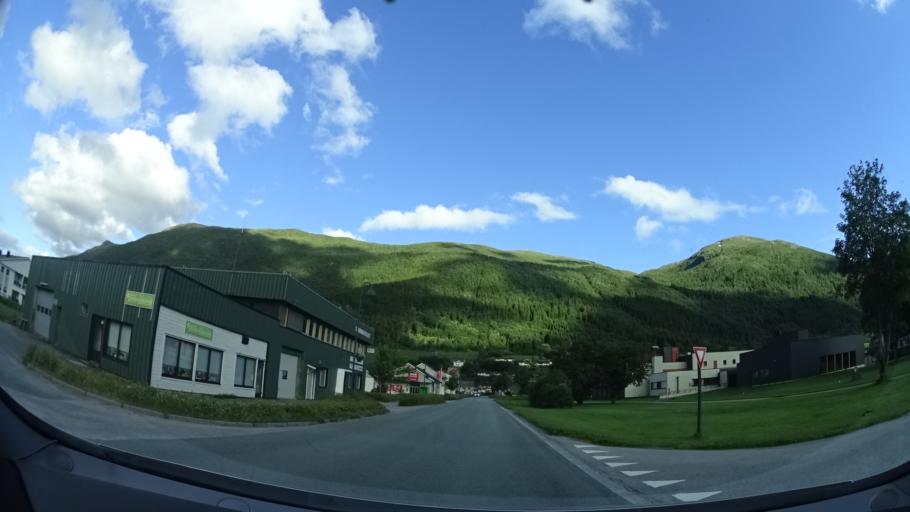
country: NO
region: More og Romsdal
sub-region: Gjemnes
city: Batnfjordsora
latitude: 62.8944
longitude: 7.6779
